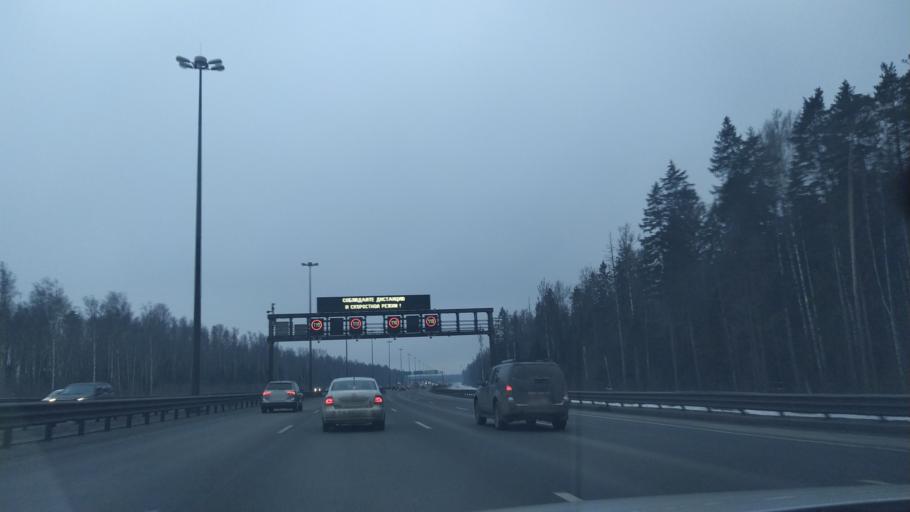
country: RU
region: Leningrad
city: Yanino Vtoroye
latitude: 59.9587
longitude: 30.5525
